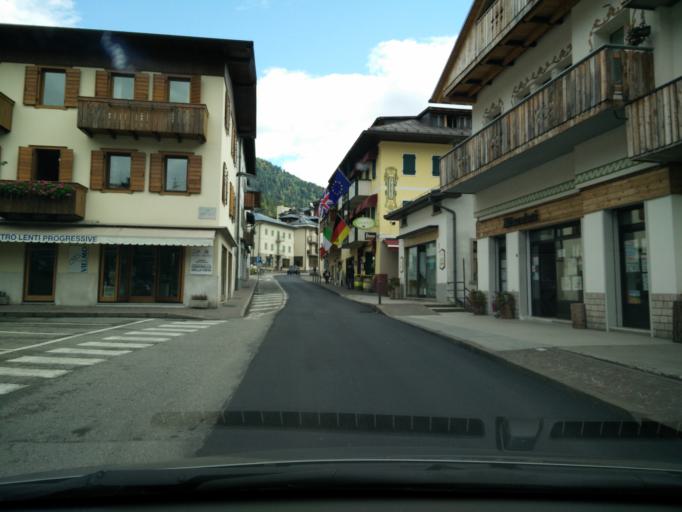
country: IT
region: Veneto
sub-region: Provincia di Belluno
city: Auronzo
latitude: 46.5523
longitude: 12.4398
